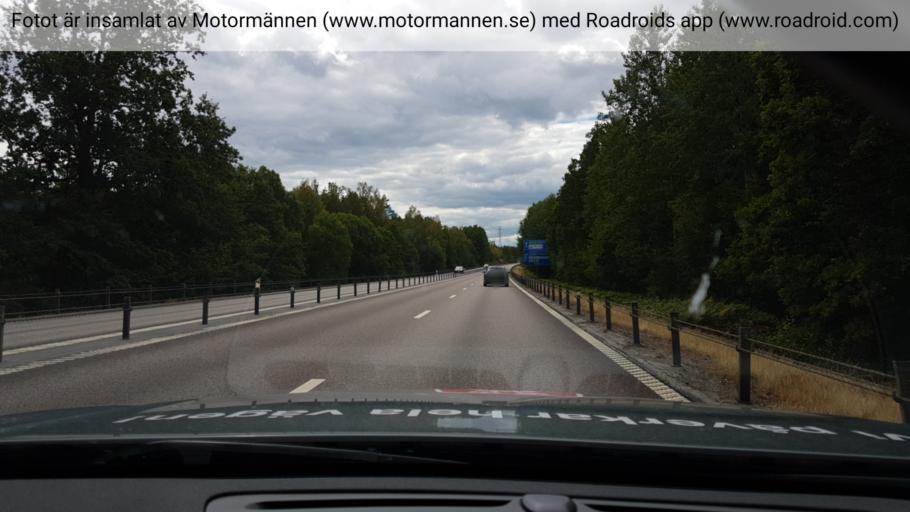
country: SE
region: Kalmar
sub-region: Oskarshamns Kommun
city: Oskarshamn
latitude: 57.2865
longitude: 16.4546
